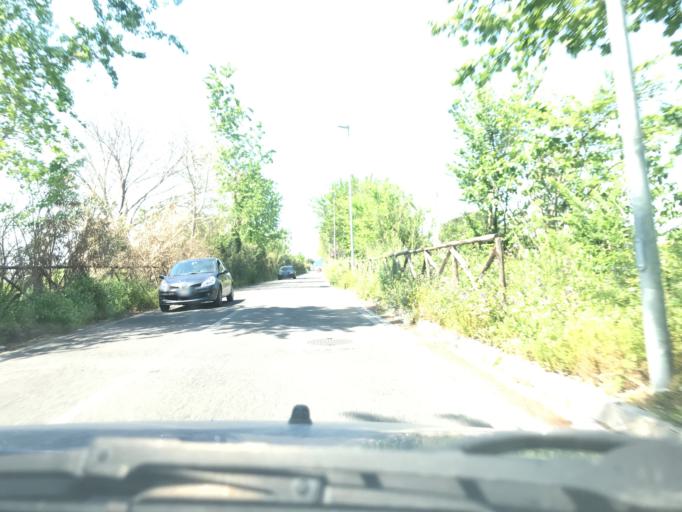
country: IT
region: Campania
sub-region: Provincia di Napoli
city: Villaricca
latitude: 40.9142
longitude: 14.1829
